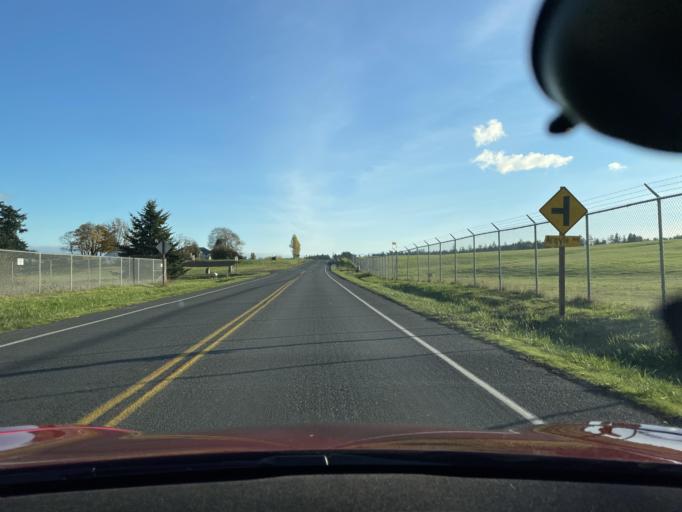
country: US
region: Washington
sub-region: San Juan County
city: Friday Harbor
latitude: 48.5226
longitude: -123.0232
